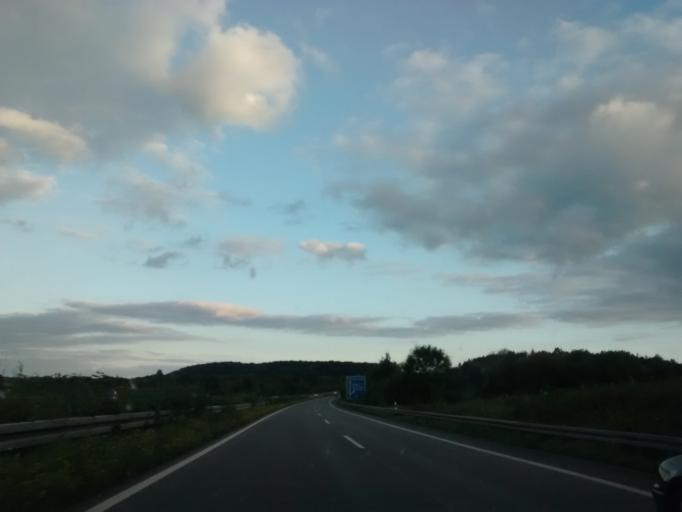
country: DE
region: Lower Saxony
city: Bissendorf
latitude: 52.2073
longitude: 8.1330
